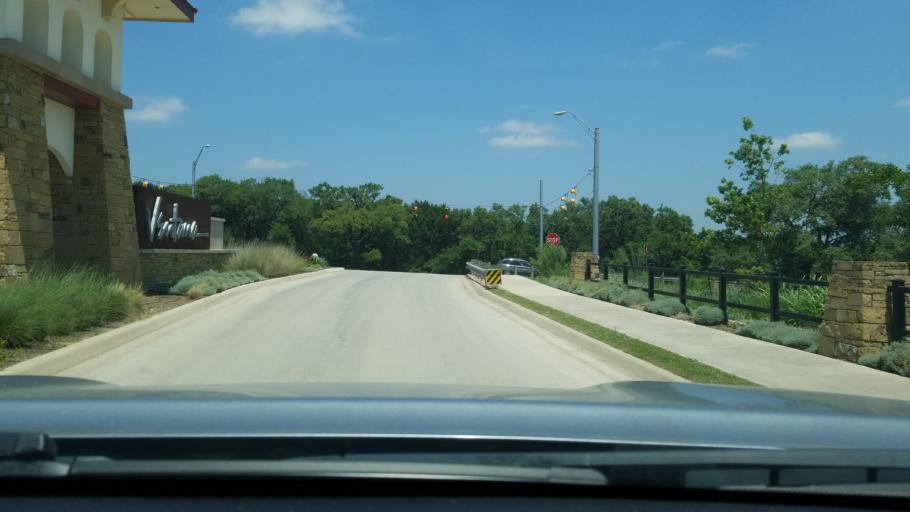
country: US
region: Texas
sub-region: Comal County
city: Bulverde
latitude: 29.8059
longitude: -98.5148
